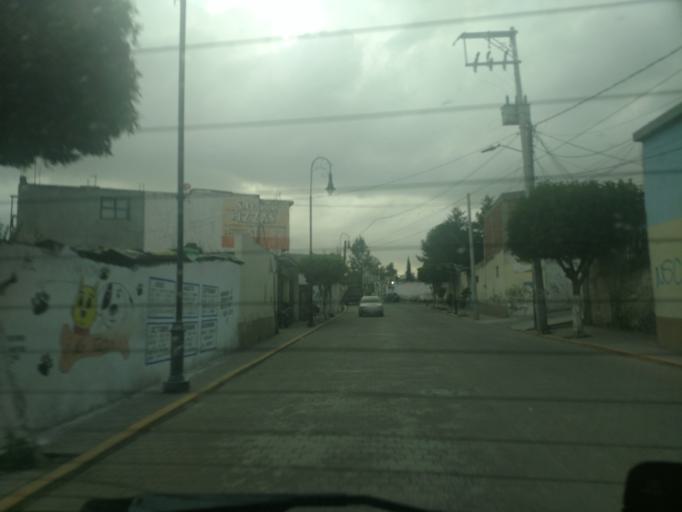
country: MX
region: Morelos
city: Coyotepec
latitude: 19.7764
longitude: -99.2125
